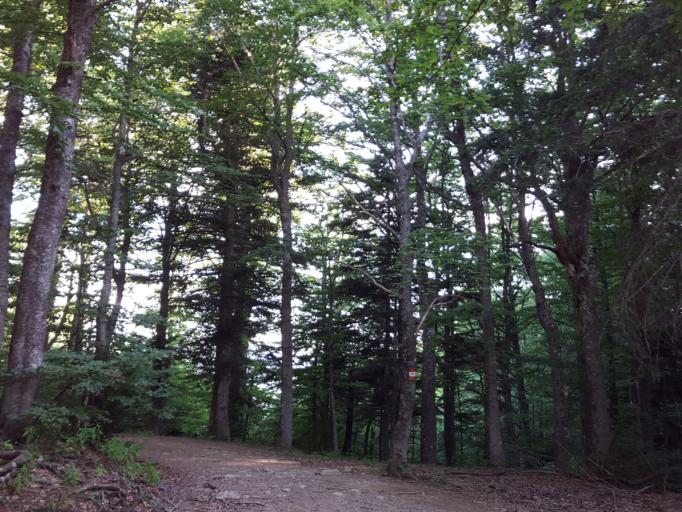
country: IT
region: Tuscany
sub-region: Provincia di Pistoia
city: Abetone
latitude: 44.1565
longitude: 10.6873
